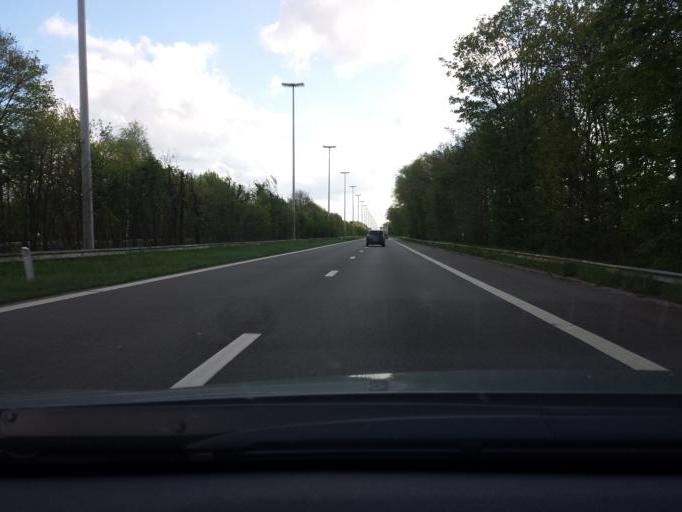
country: BE
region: Wallonia
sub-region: Province de Liege
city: Lontzen
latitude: 50.6666
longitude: 6.0269
